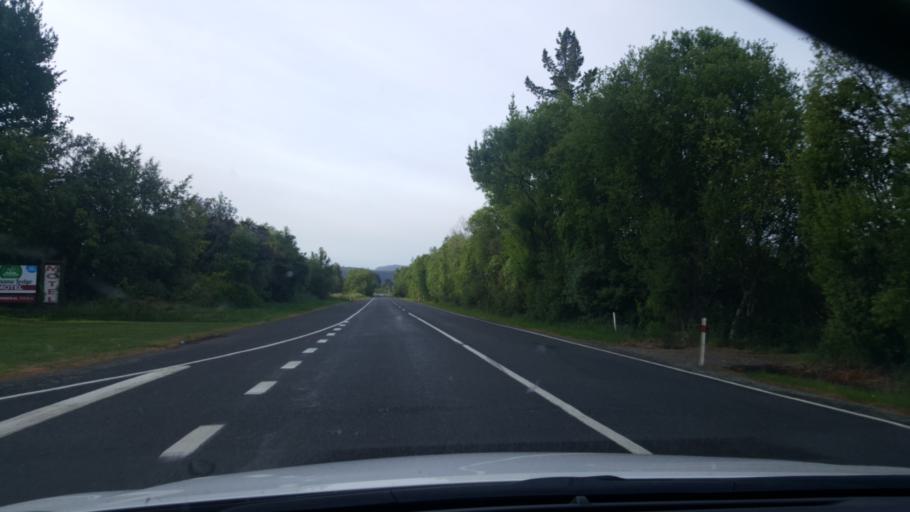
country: NZ
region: Waikato
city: Turangi
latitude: -38.9690
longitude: 175.7688
